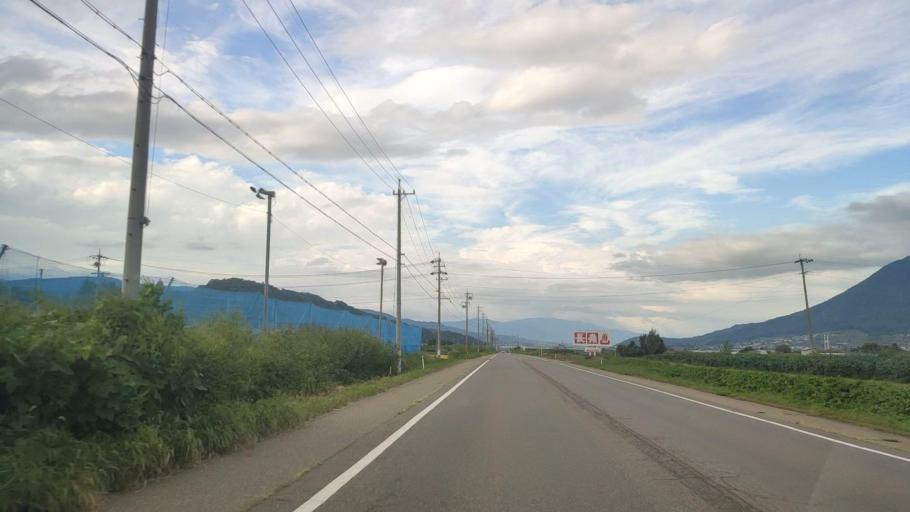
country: JP
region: Nagano
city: Nakano
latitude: 36.7719
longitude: 138.3505
